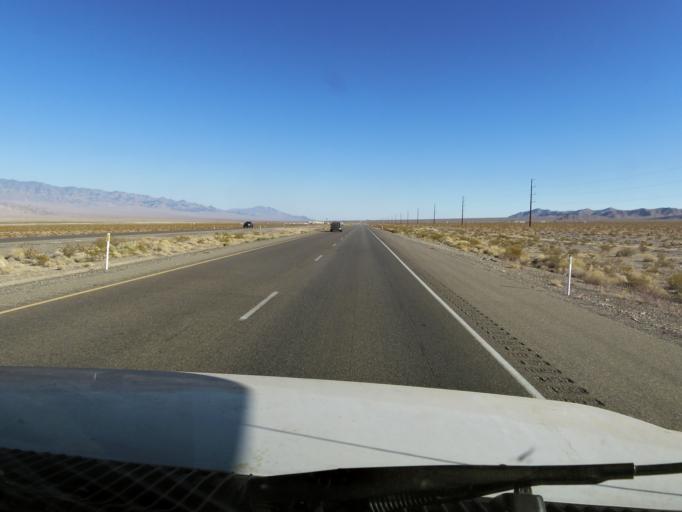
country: US
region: Nevada
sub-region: Clark County
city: Summerlin South
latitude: 36.5425
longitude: -115.5811
